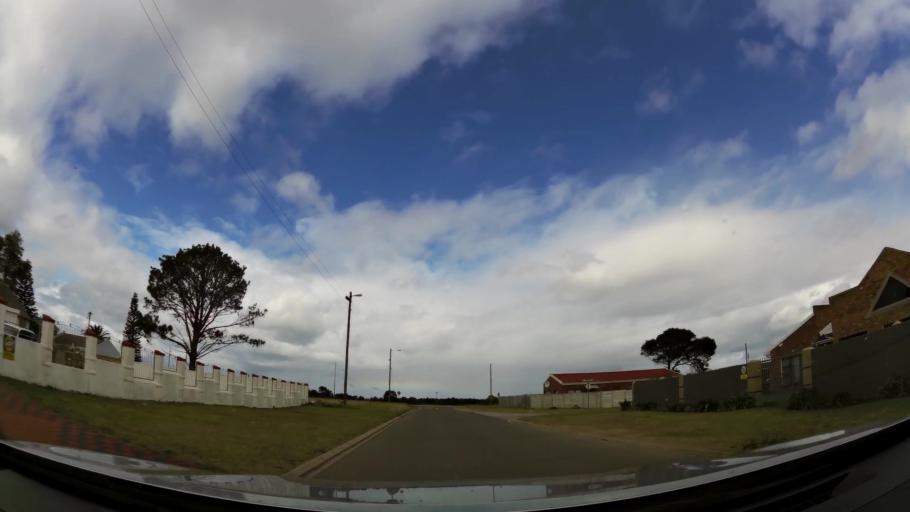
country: ZA
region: Western Cape
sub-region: Eden District Municipality
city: George
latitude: -34.0092
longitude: 22.4393
